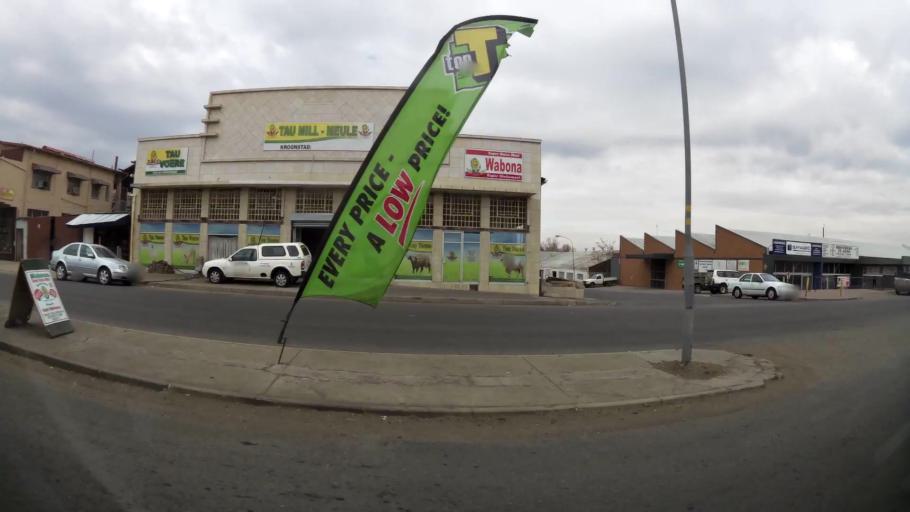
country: ZA
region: Orange Free State
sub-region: Fezile Dabi District Municipality
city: Kroonstad
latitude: -27.6630
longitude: 27.2310
